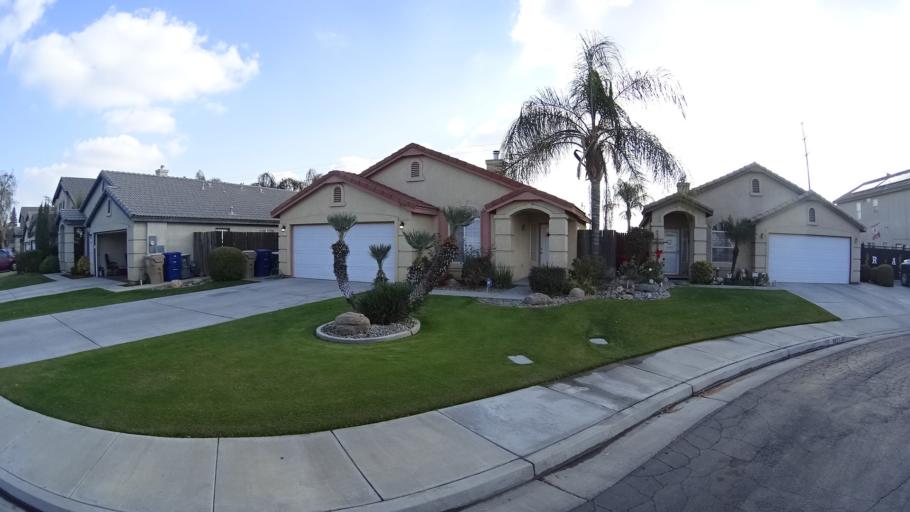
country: US
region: California
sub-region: Kern County
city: Greenacres
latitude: 35.3115
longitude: -119.1094
